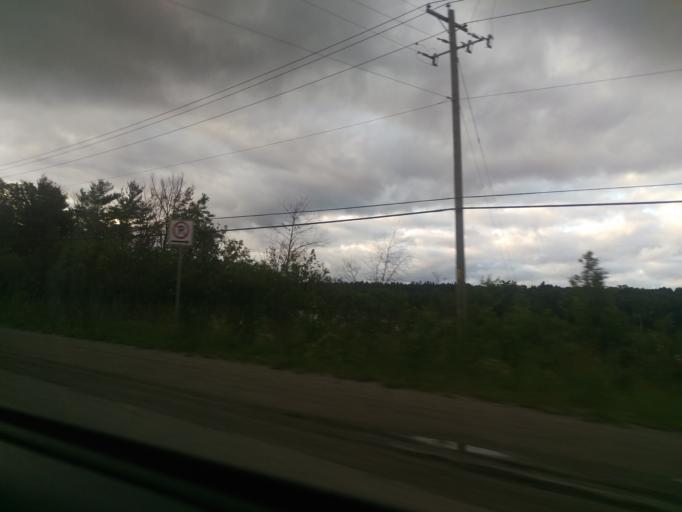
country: CA
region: Quebec
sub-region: Outaouais
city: Gatineau
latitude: 45.4802
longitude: -75.7459
